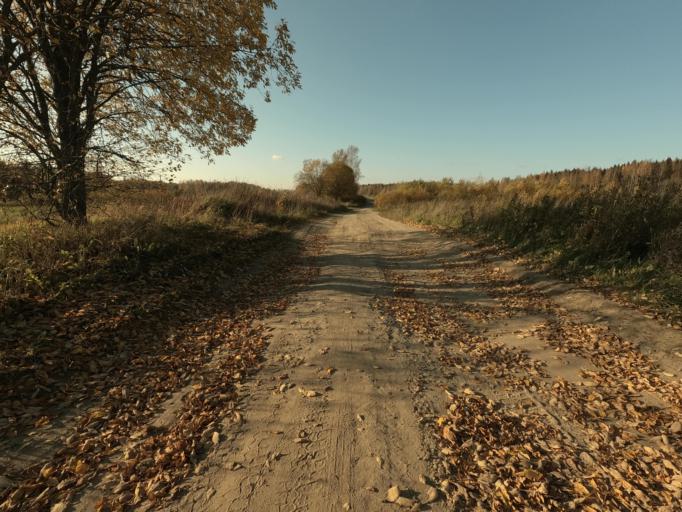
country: RU
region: Leningrad
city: Luppolovo
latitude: 60.1442
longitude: 30.2464
